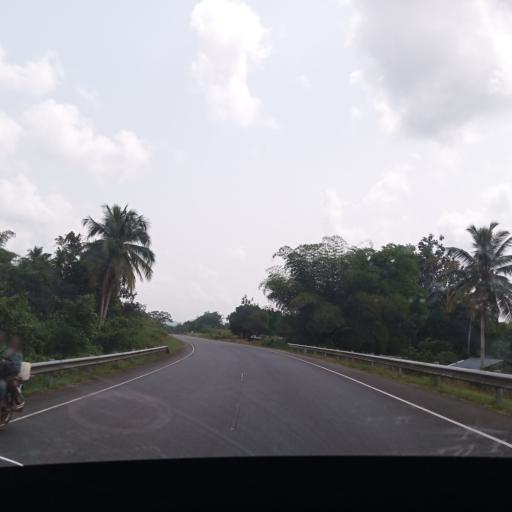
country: LR
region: Margibi
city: Kakata
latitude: 6.2445
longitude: -10.2911
